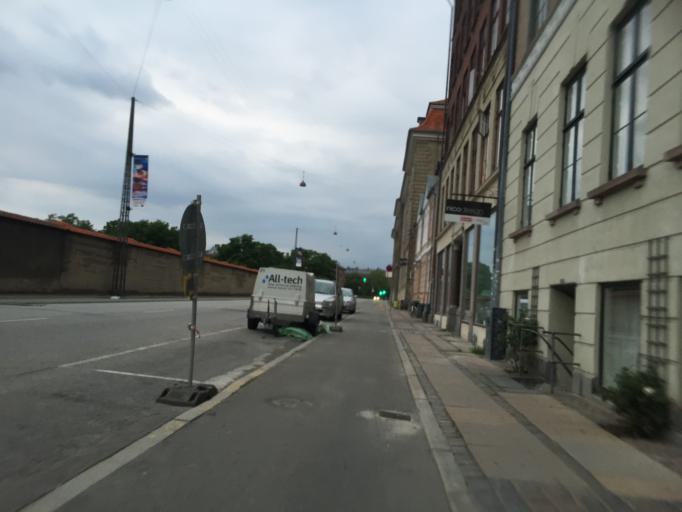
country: DK
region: Capital Region
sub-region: Kobenhavn
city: Copenhagen
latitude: 55.6868
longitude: 12.5812
